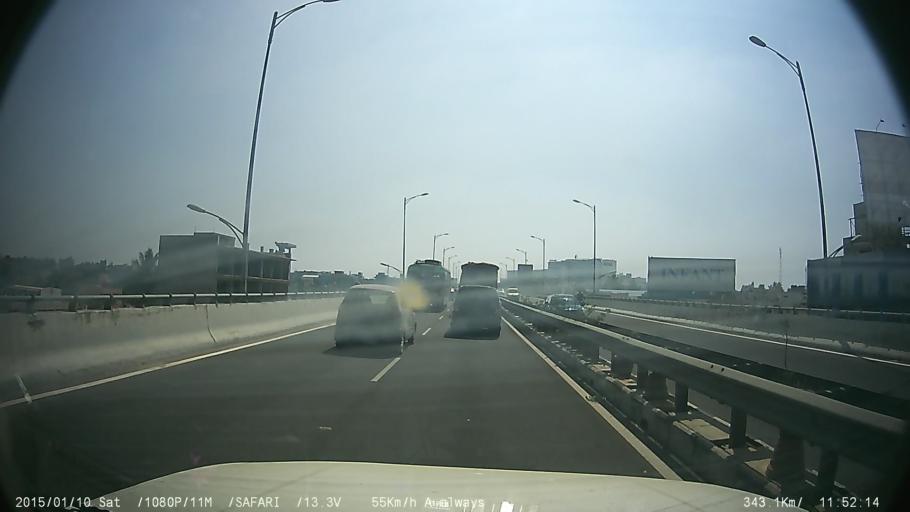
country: IN
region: Karnataka
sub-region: Bangalore Urban
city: Bangalore
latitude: 12.8969
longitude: 77.6352
